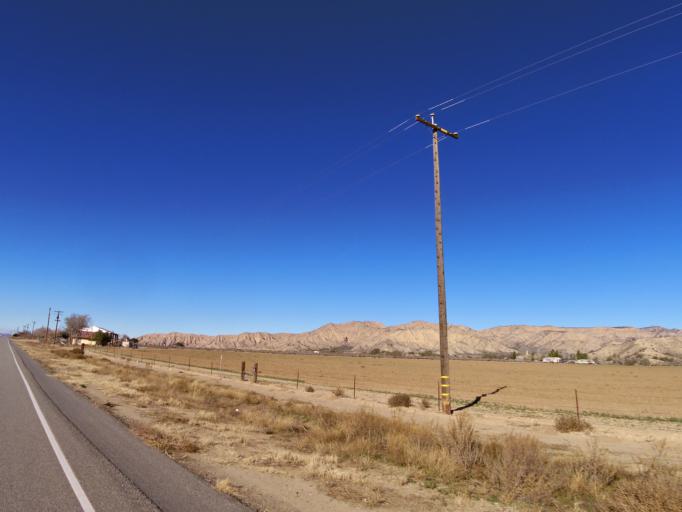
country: US
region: California
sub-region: Kern County
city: Maricopa
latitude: 34.8084
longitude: -119.4549
